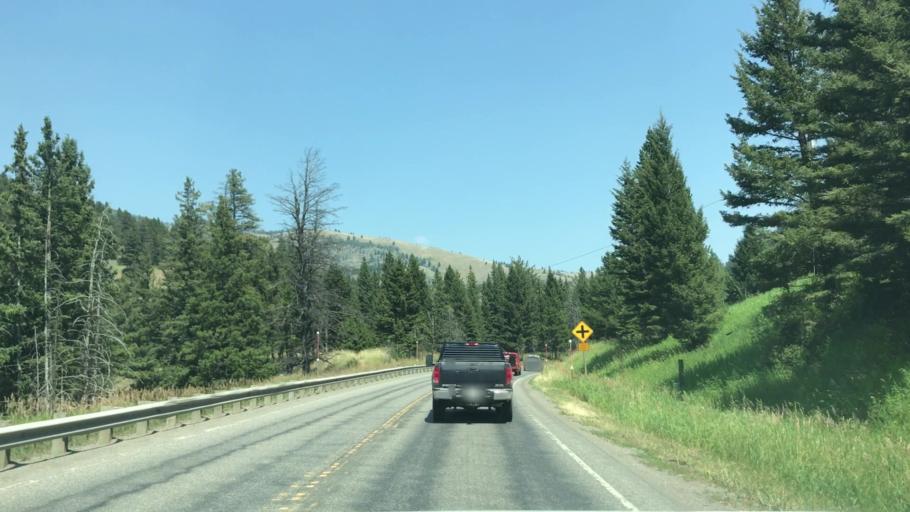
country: US
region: Montana
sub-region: Gallatin County
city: Big Sky
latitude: 45.2865
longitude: -111.2217
